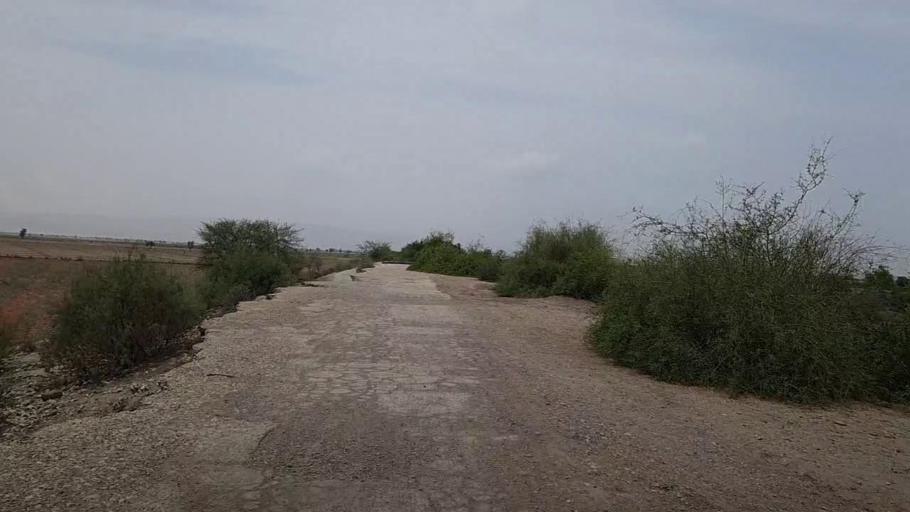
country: PK
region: Sindh
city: Sann
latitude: 26.2090
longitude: 67.9642
